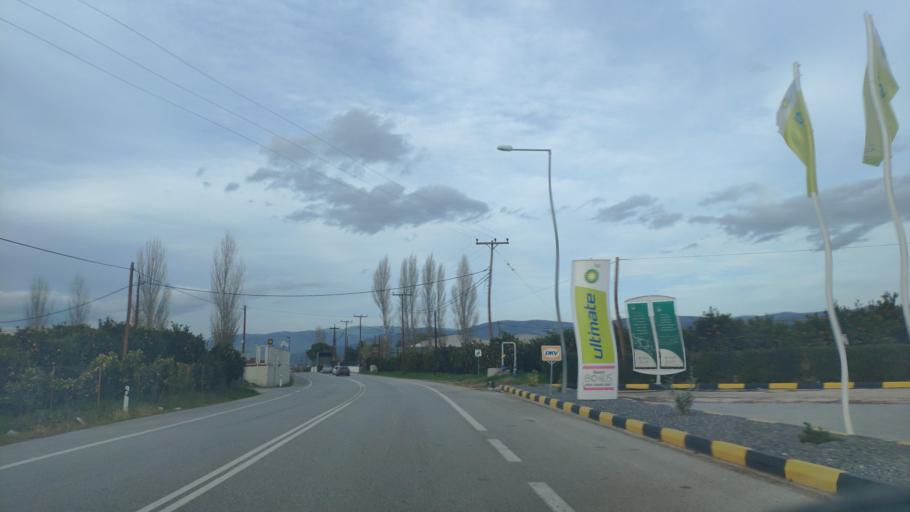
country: GR
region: Peloponnese
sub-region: Nomos Argolidos
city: Nea Tirins
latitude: 37.6107
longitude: 22.8121
